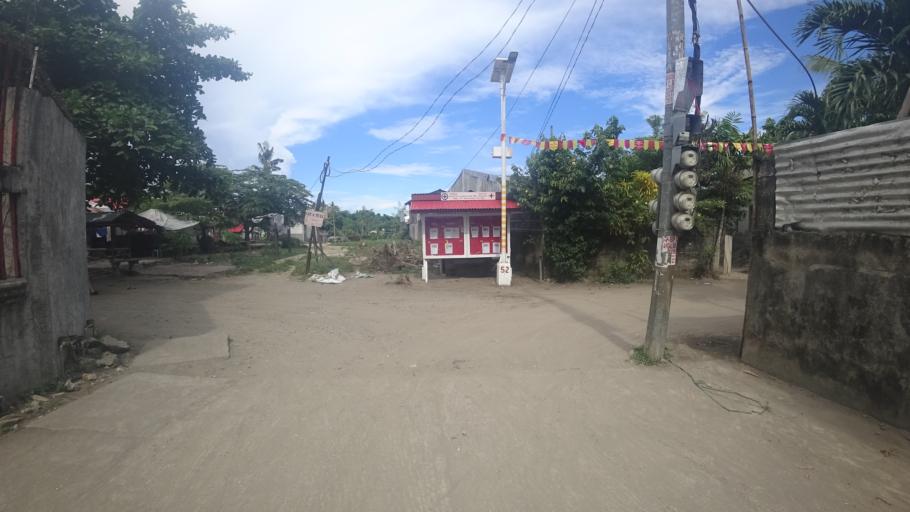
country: PH
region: Eastern Visayas
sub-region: Province of Leyte
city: Baras
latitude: 11.2036
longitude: 125.0108
